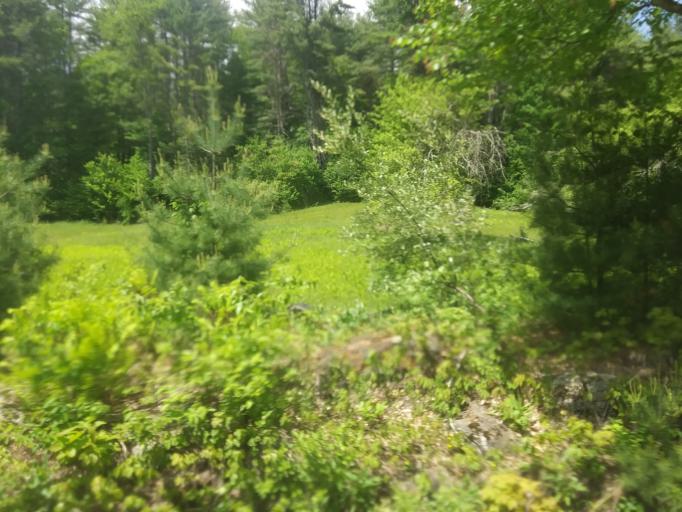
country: US
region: Massachusetts
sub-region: Franklin County
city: Buckland
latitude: 42.5894
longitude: -72.7701
